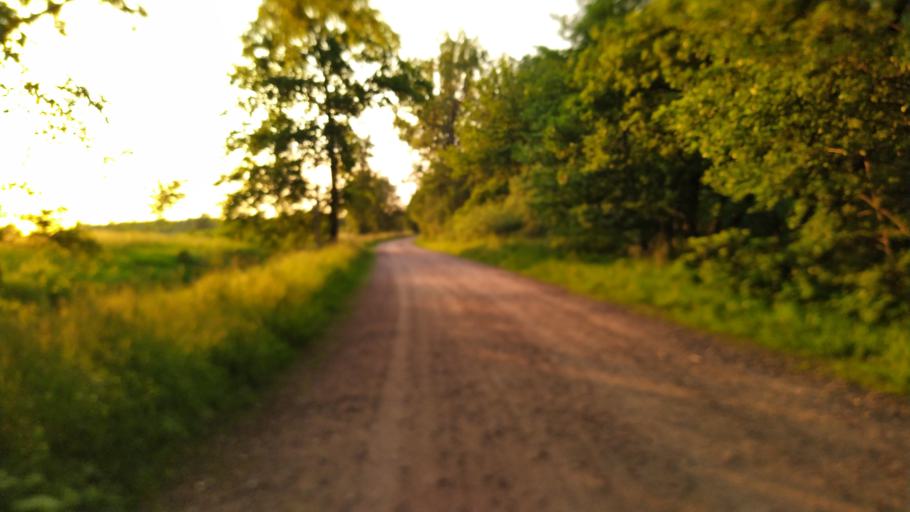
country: DE
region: Lower Saxony
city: Neu Wulmstorf
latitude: 53.4827
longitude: 9.8280
